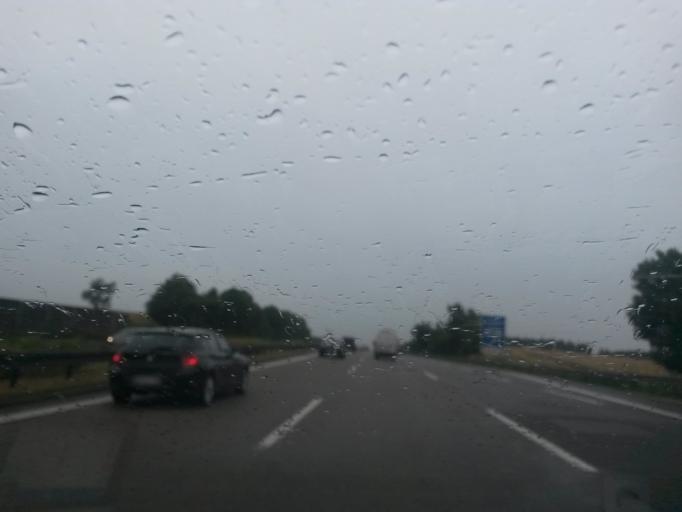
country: DE
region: Bavaria
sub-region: Upper Bavaria
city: Hepberg
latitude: 48.8320
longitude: 11.4723
